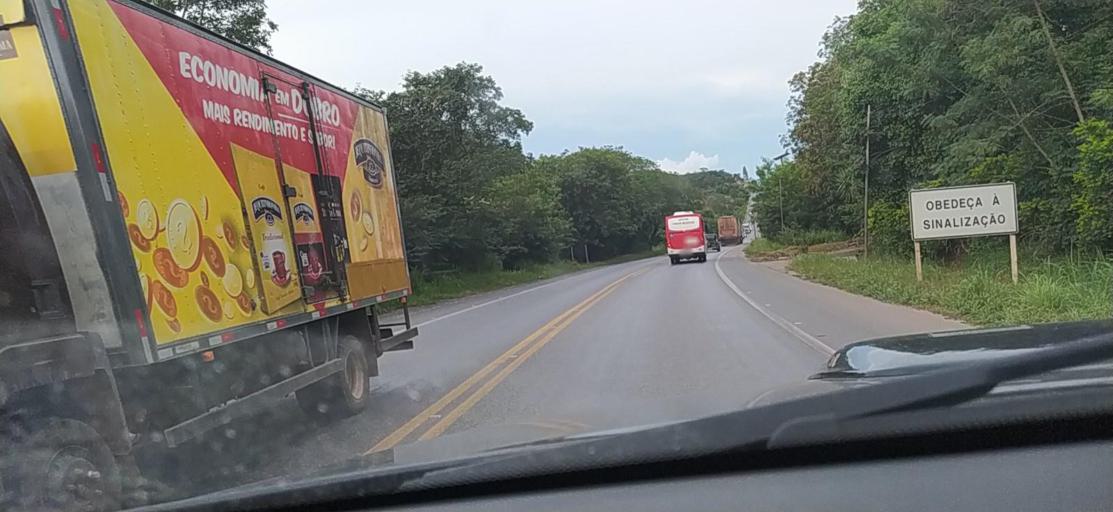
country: BR
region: Minas Gerais
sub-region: Montes Claros
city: Montes Claros
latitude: -16.6742
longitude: -43.7976
